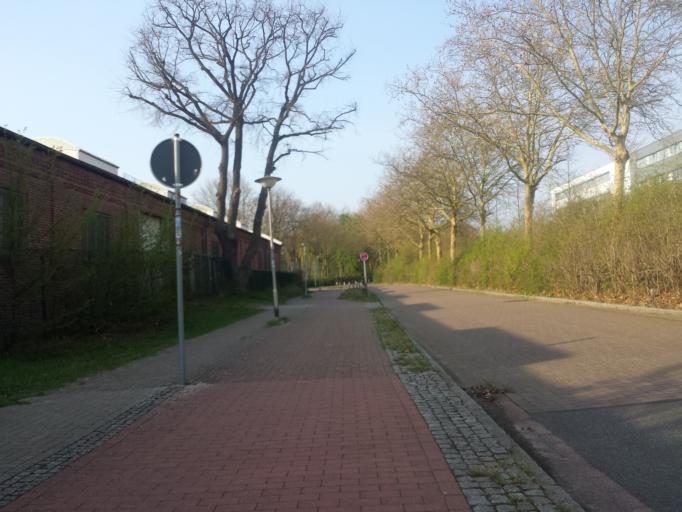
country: DE
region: Lower Saxony
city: Lilienthal
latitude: 53.0612
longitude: 8.9006
